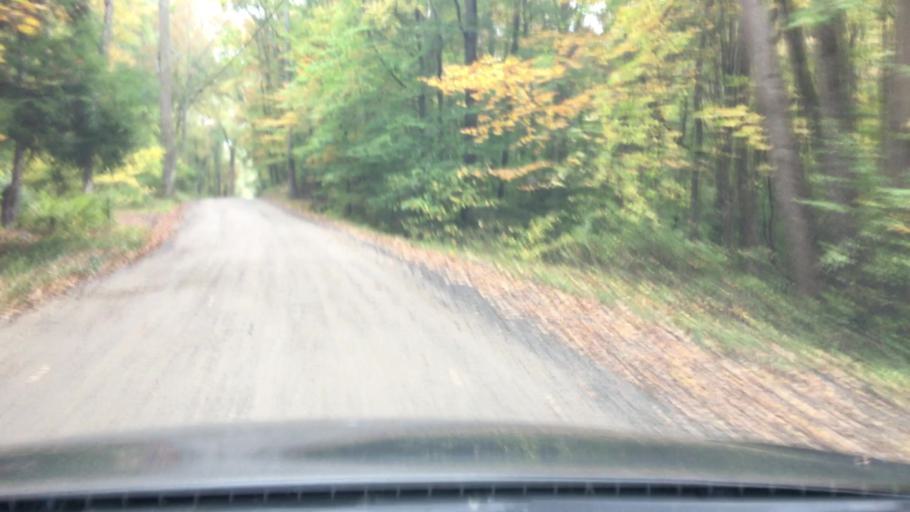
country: US
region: Connecticut
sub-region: New Haven County
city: Heritage Village
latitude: 41.5117
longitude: -73.2741
